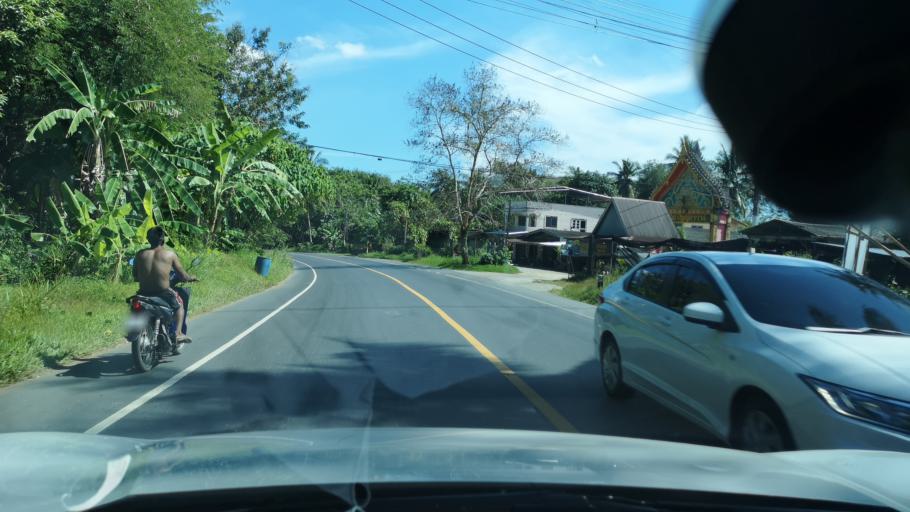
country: TH
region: Phangnga
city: Phang Nga
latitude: 8.5345
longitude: 98.5022
